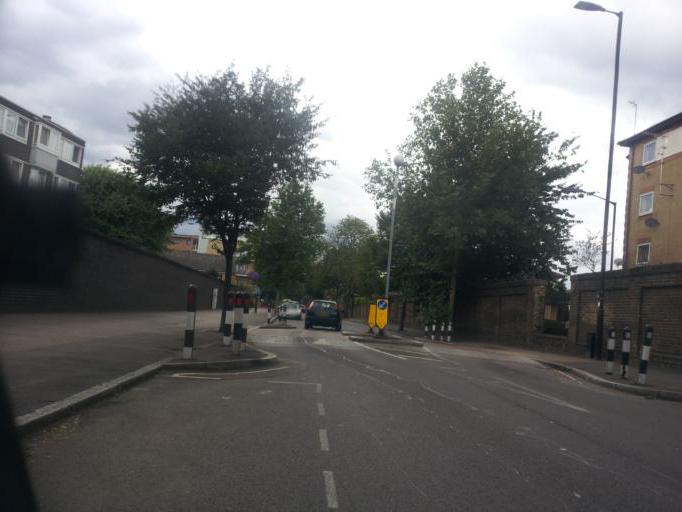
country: GB
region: England
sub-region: Greater London
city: Camberwell
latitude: 51.4883
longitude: -0.0695
